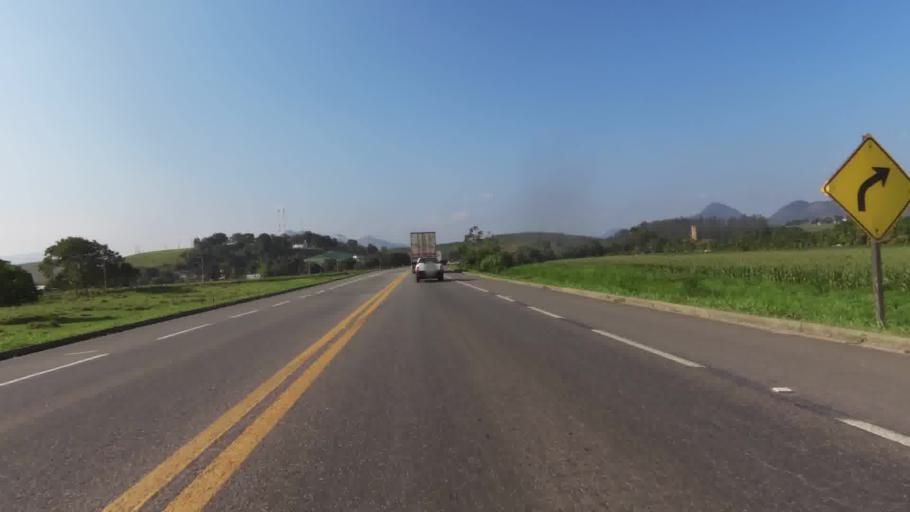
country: BR
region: Espirito Santo
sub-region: Alfredo Chaves
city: Alfredo Chaves
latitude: -20.6904
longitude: -40.6817
